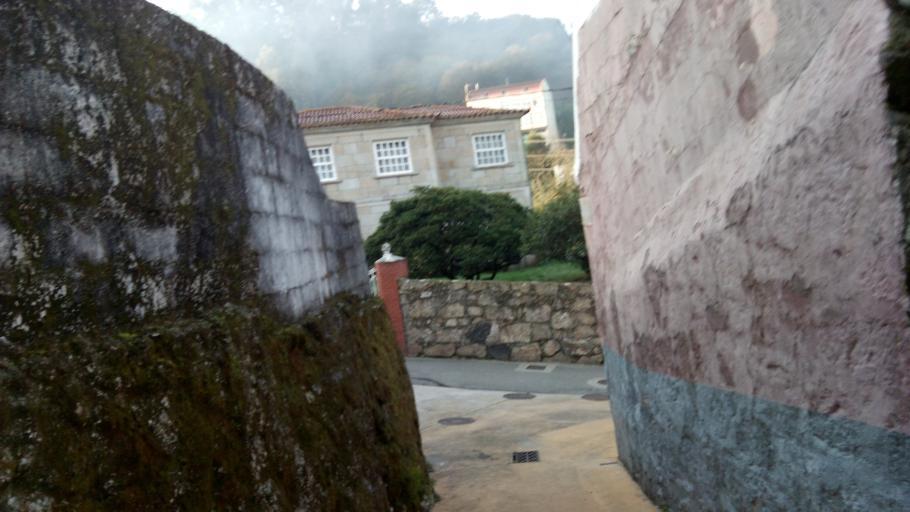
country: ES
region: Galicia
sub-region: Provincia de Pontevedra
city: Marin
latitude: 42.3893
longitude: -8.7032
